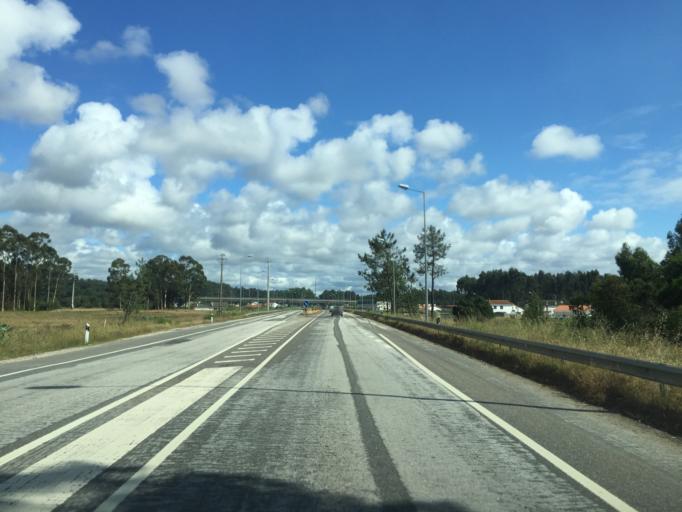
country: PT
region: Coimbra
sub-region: Figueira da Foz
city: Lavos
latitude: 40.0545
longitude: -8.8665
